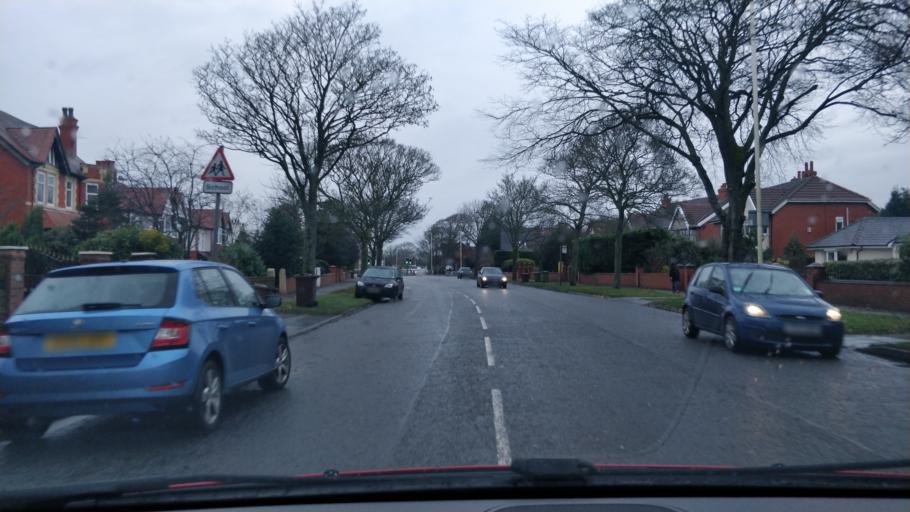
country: GB
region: England
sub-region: Sefton
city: Formby
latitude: 53.5976
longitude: -3.0357
